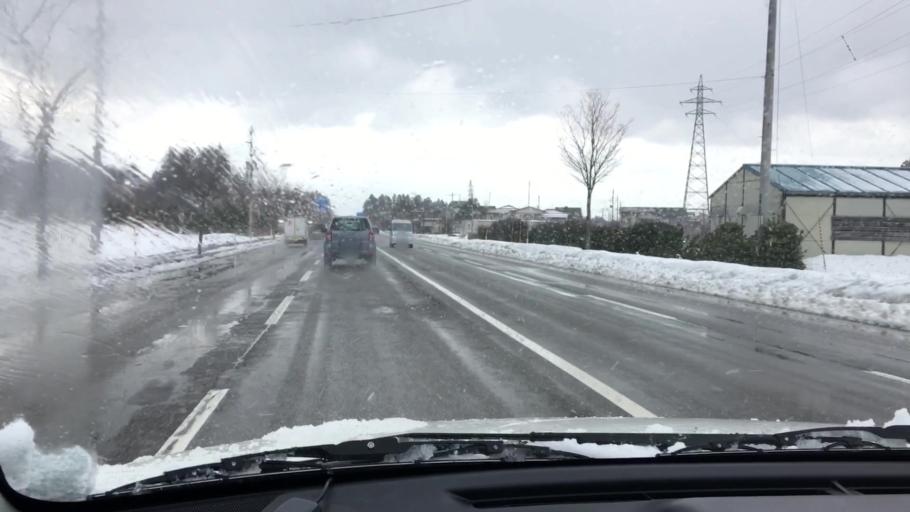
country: JP
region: Niigata
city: Joetsu
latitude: 37.1001
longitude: 138.2310
